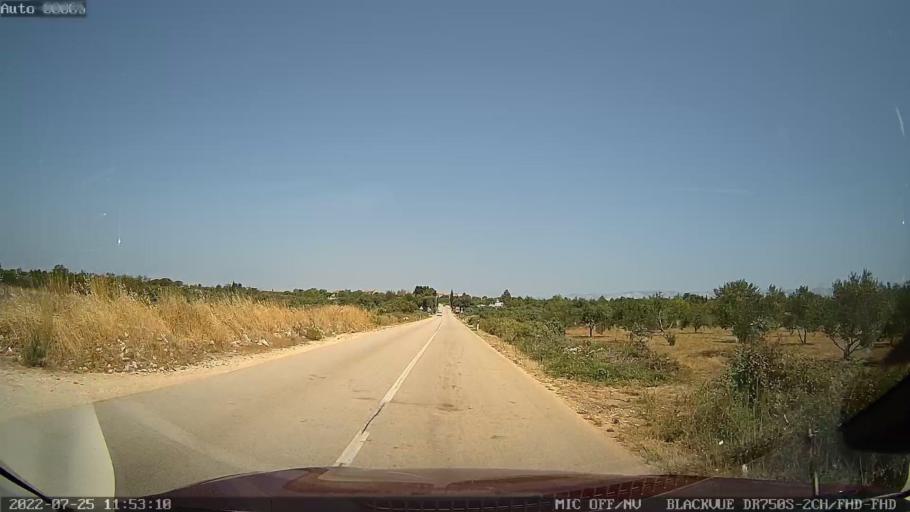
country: HR
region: Zadarska
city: Vrsi
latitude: 44.2537
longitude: 15.2362
